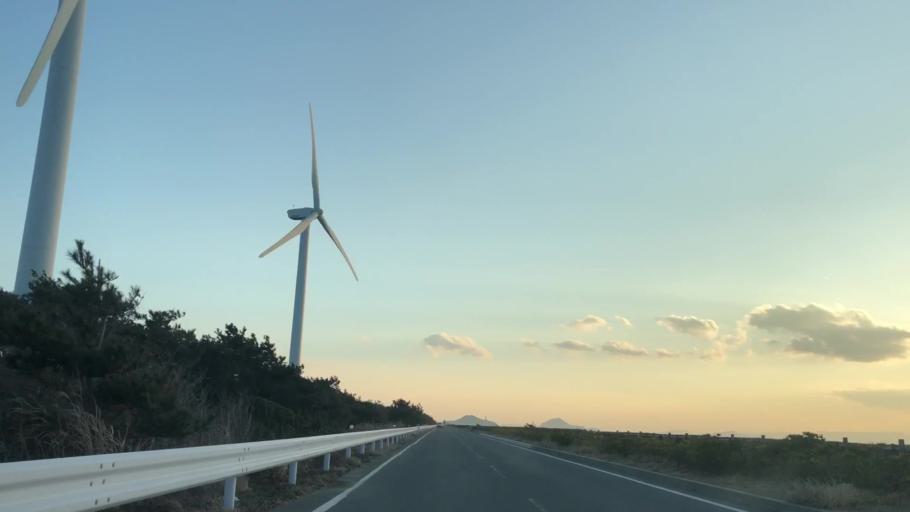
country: JP
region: Aichi
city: Toyohama
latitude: 34.6387
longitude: 137.0526
